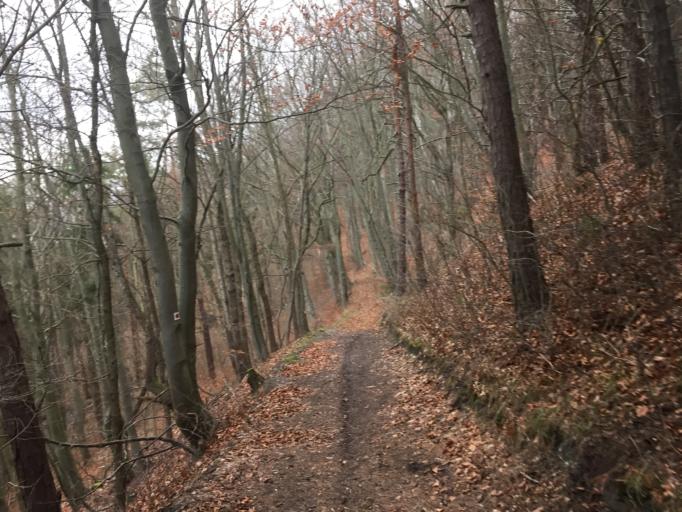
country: DE
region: Thuringia
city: Bad Blankenburg
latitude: 50.6944
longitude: 11.2750
